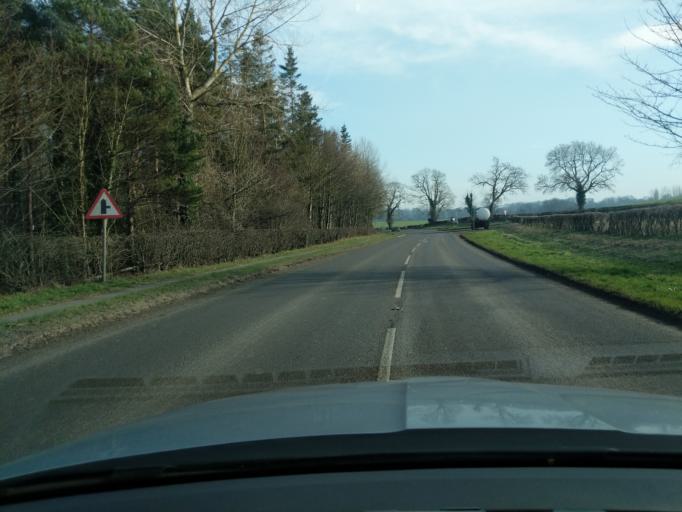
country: GB
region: England
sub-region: North Yorkshire
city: Bedale
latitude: 54.2963
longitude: -1.6128
